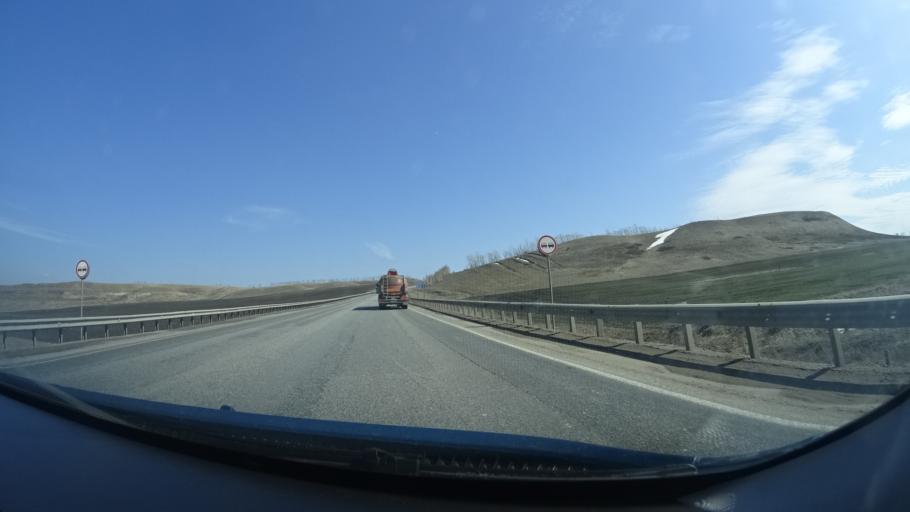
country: RU
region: Bashkortostan
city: Serafimovskiy
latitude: 54.4705
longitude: 53.7622
